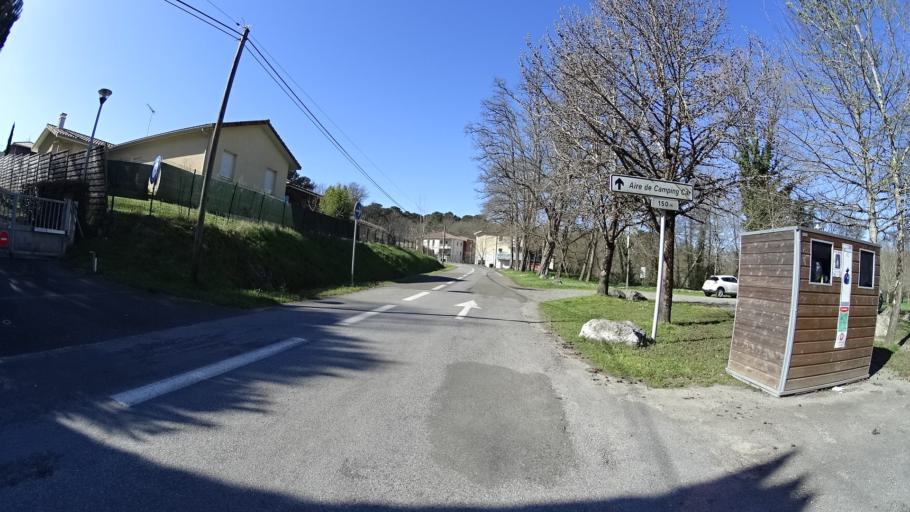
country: FR
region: Aquitaine
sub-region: Departement des Landes
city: Saint-Paul-les-Dax
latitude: 43.7326
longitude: -1.0730
